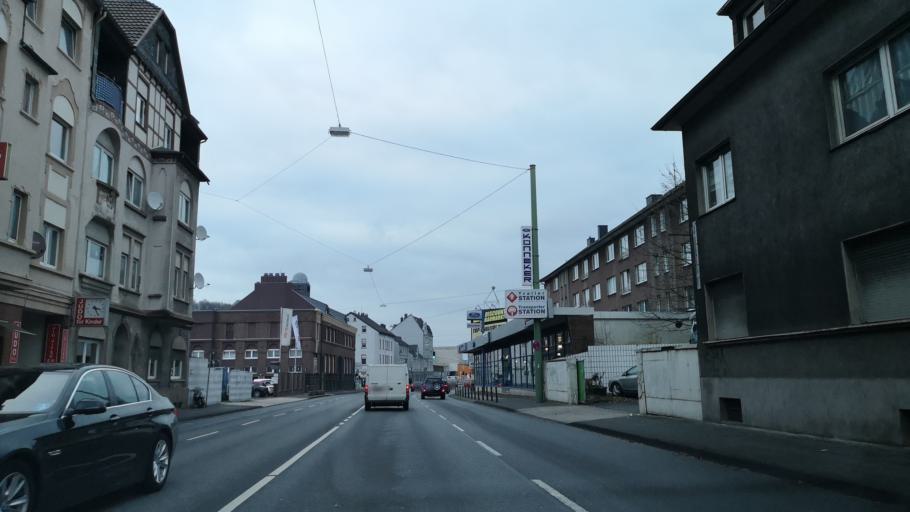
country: DE
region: North Rhine-Westphalia
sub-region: Regierungsbezirk Arnsberg
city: Hagen
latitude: 51.3515
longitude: 7.4425
